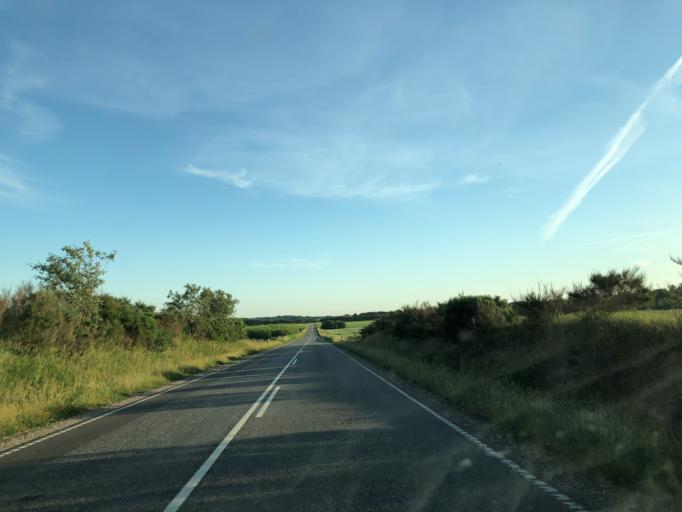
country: DK
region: Central Jutland
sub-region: Struer Kommune
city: Struer
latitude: 56.4250
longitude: 8.5066
